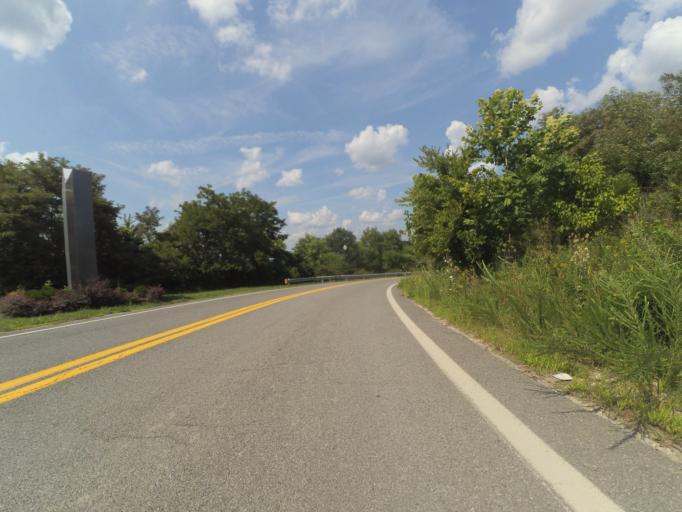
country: US
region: West Virginia
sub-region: Cabell County
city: Huntington
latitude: 38.3949
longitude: -82.4238
